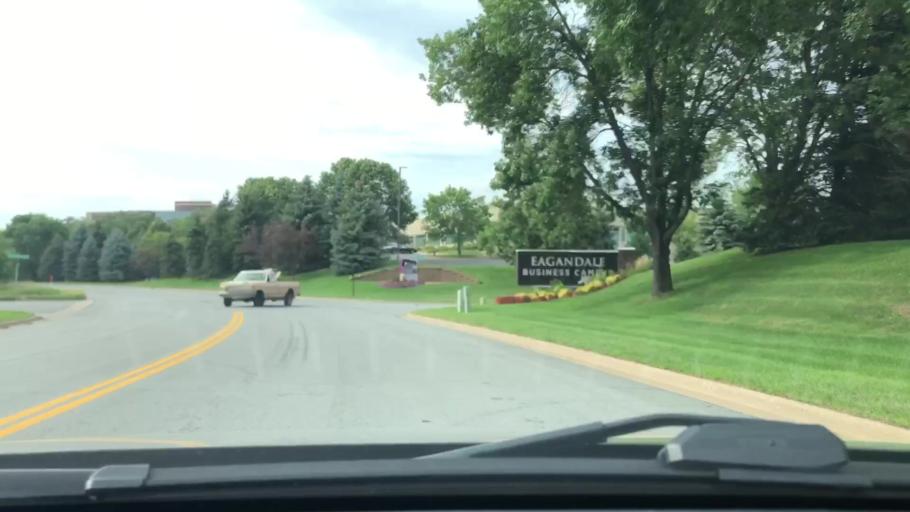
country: US
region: Minnesota
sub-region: Dakota County
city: Mendota Heights
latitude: 44.8569
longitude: -93.1608
